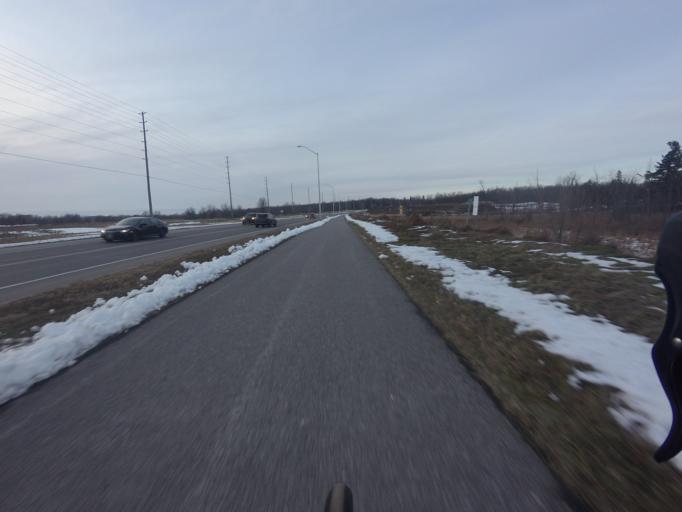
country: CA
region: Ontario
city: Bells Corners
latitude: 45.3195
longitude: -75.9468
